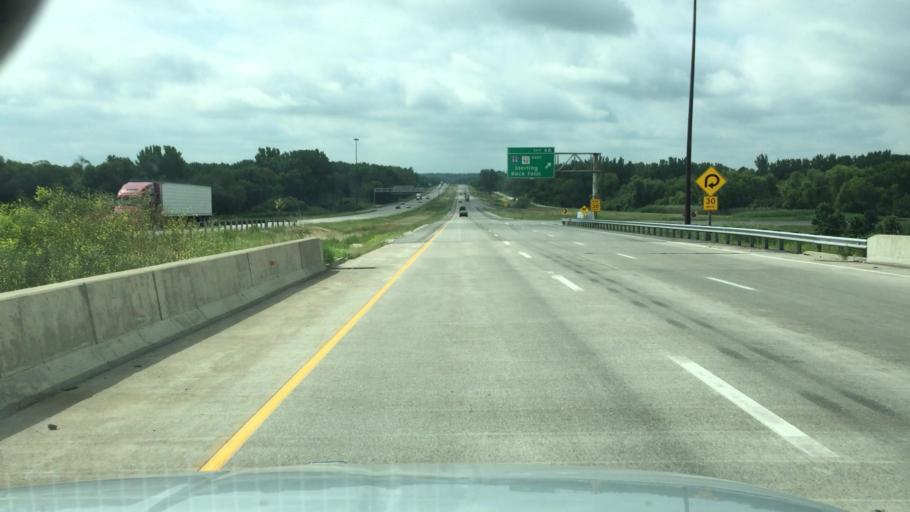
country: US
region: Illinois
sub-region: Henry County
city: Colona
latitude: 41.5358
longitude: -90.3417
